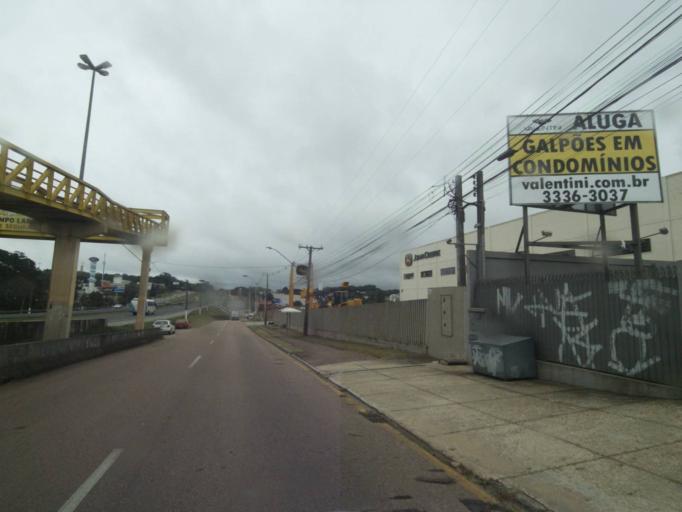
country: BR
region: Parana
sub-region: Curitiba
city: Curitiba
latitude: -25.4304
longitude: -49.3334
